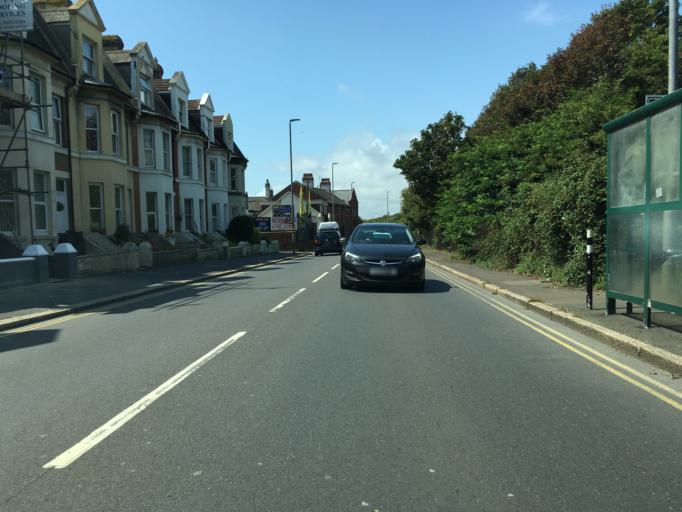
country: GB
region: England
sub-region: East Sussex
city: Saint Leonards-on-Sea
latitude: 50.8512
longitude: 0.5359
